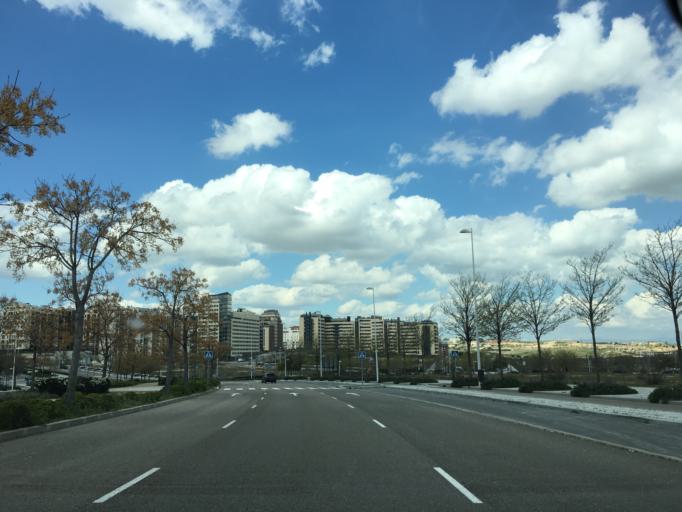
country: ES
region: Madrid
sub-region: Provincia de Madrid
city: Hortaleza
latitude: 40.4918
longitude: -3.6104
